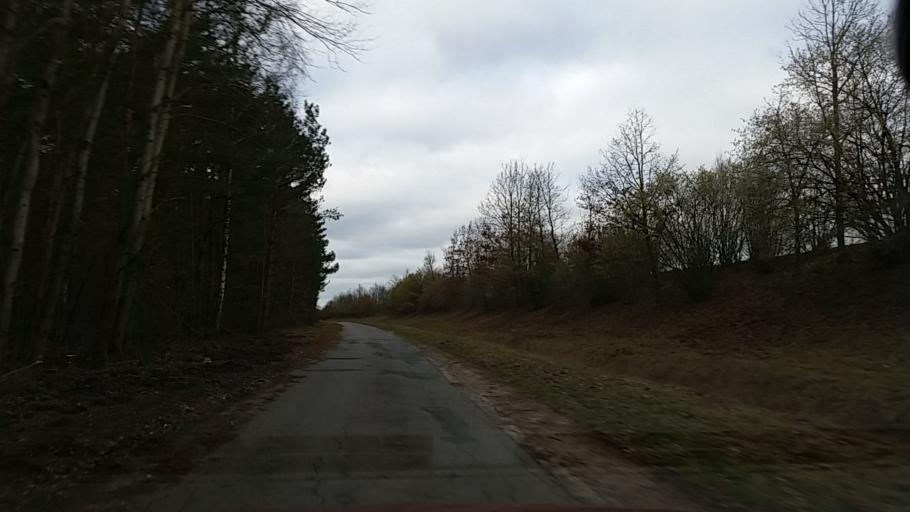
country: DE
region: Lower Saxony
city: Wieren
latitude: 52.8702
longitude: 10.6543
